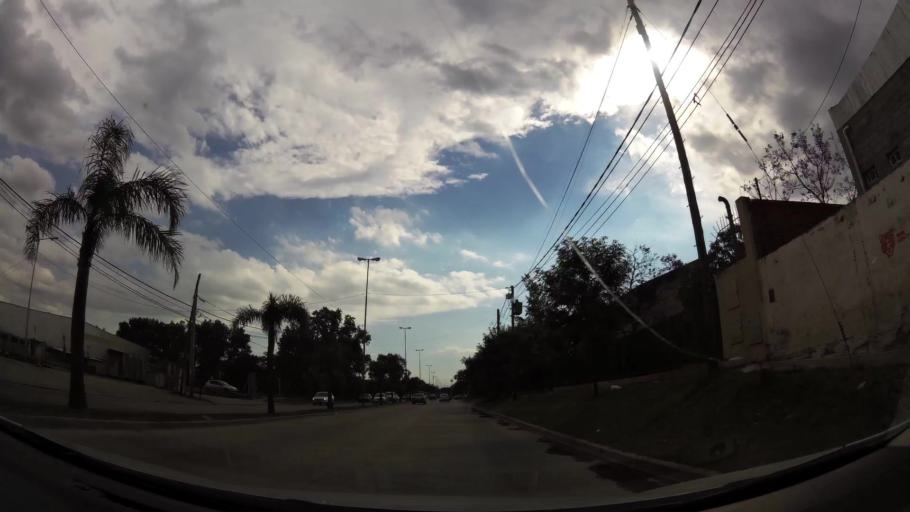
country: AR
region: Buenos Aires
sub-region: Partido de Tigre
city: Tigre
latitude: -34.4820
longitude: -58.6086
